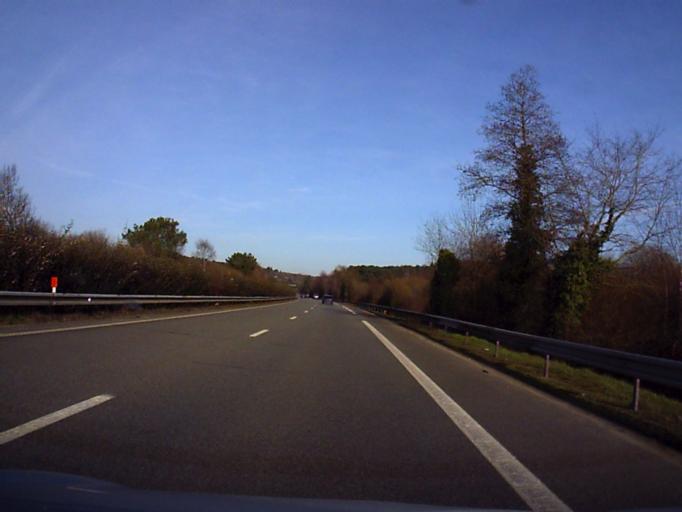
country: FR
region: Brittany
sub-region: Departement du Morbihan
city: Saint-Nolff
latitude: 47.6730
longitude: -2.6813
